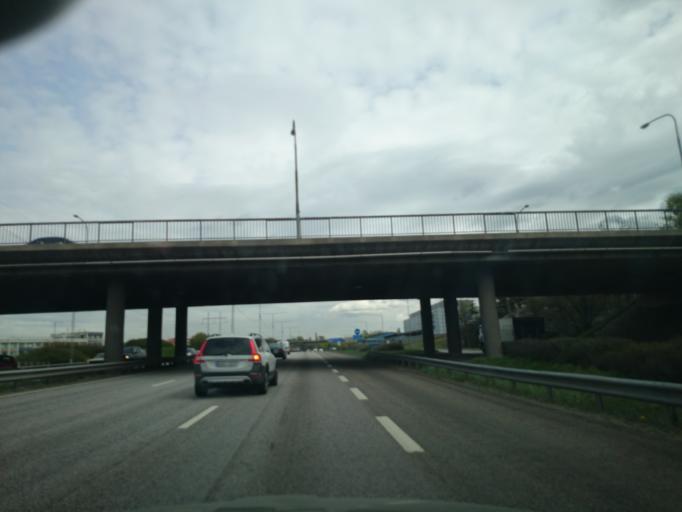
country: SE
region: Stockholm
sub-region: Huddinge Kommun
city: Segeltorp
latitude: 59.2872
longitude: 17.9479
